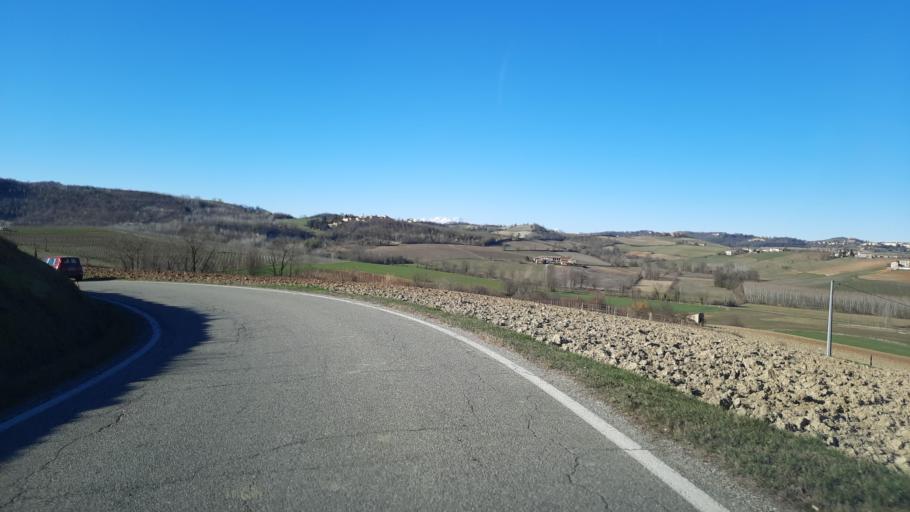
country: IT
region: Piedmont
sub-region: Provincia di Alessandria
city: Frassinello Monferrato
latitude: 45.0400
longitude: 8.3799
